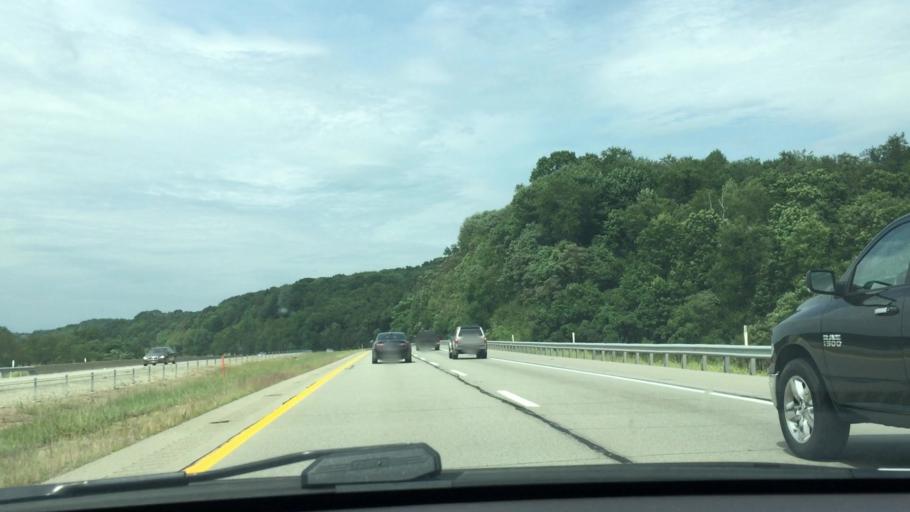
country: US
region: Pennsylvania
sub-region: Allegheny County
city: Franklin Park
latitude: 40.5683
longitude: -80.0900
